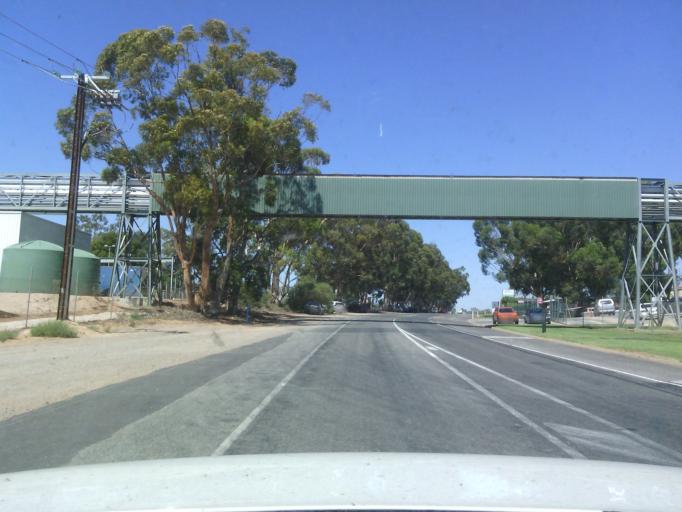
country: AU
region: South Australia
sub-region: Berri and Barmera
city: Monash
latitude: -34.2786
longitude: 140.5431
